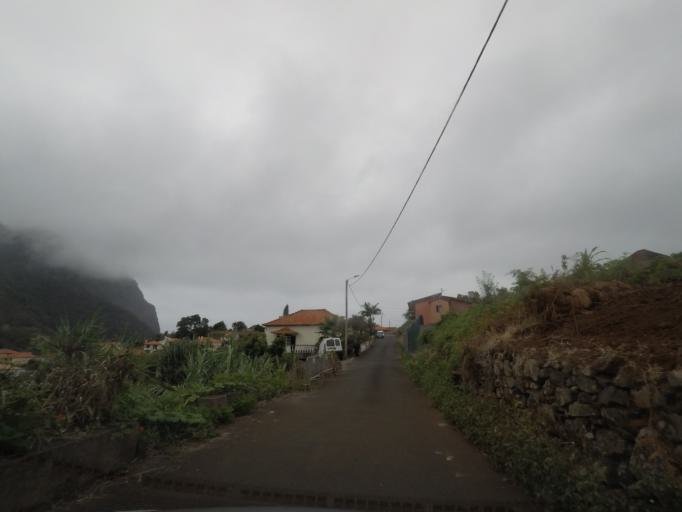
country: PT
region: Madeira
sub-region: Santana
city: Santana
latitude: 32.7679
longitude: -16.8455
